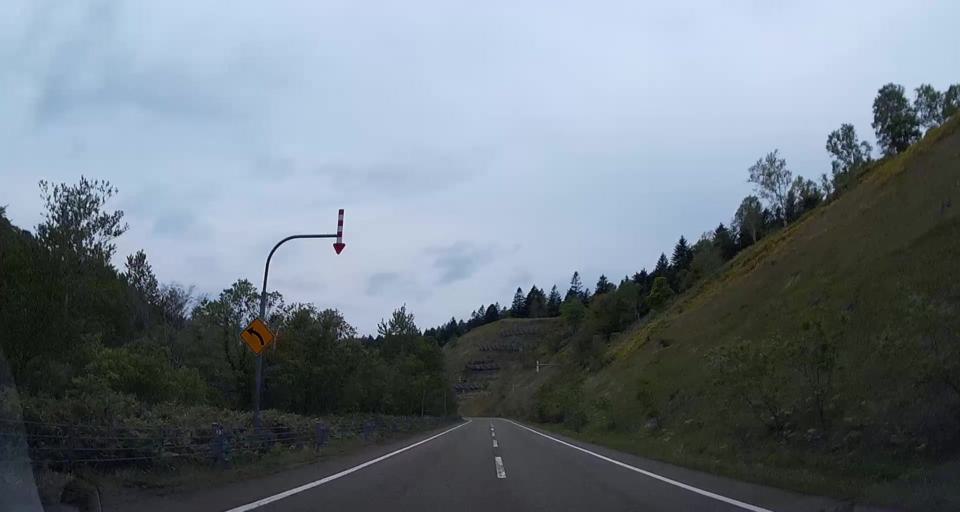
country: JP
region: Hokkaido
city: Shiraoi
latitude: 42.6776
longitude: 141.1279
